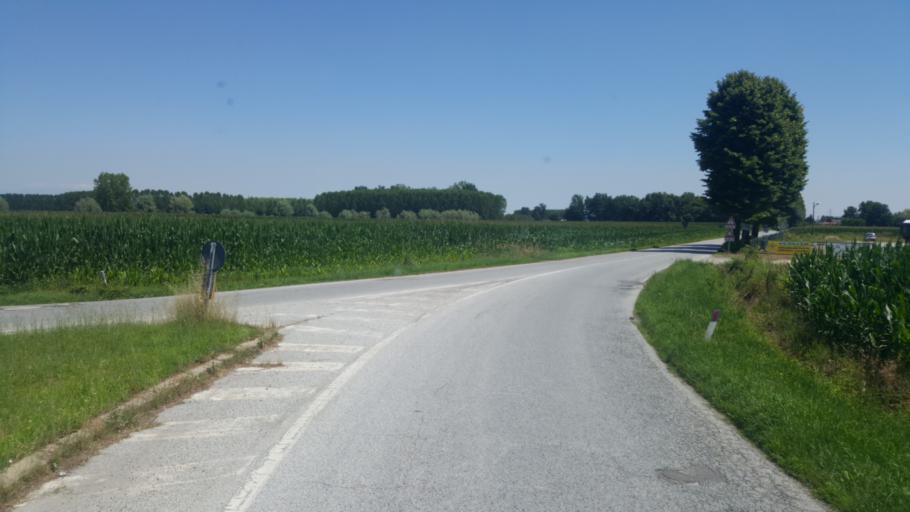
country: IT
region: Piedmont
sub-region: Provincia di Torino
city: Airasca
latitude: 44.9191
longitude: 7.4960
